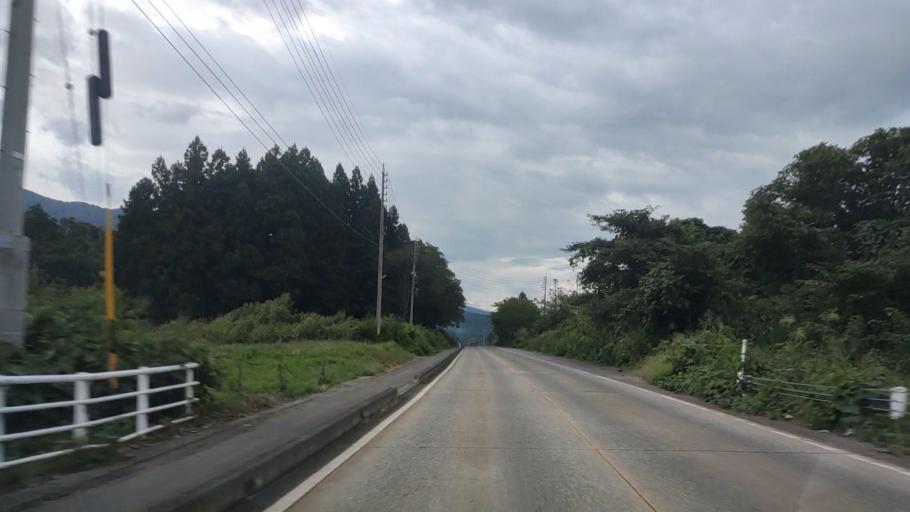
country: JP
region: Nagano
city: Iiyama
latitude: 36.8893
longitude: 138.4084
